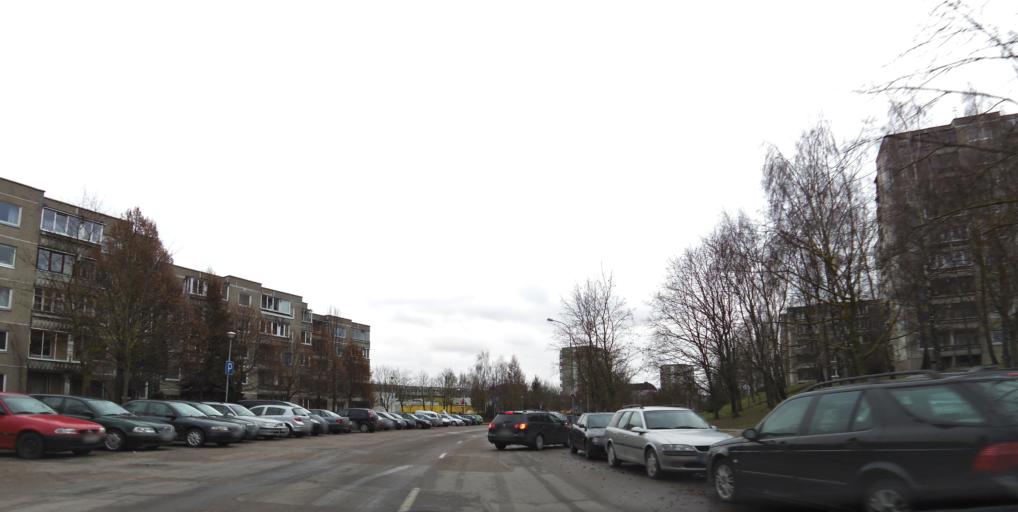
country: LT
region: Vilnius County
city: Justiniskes
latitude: 54.7202
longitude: 25.2289
